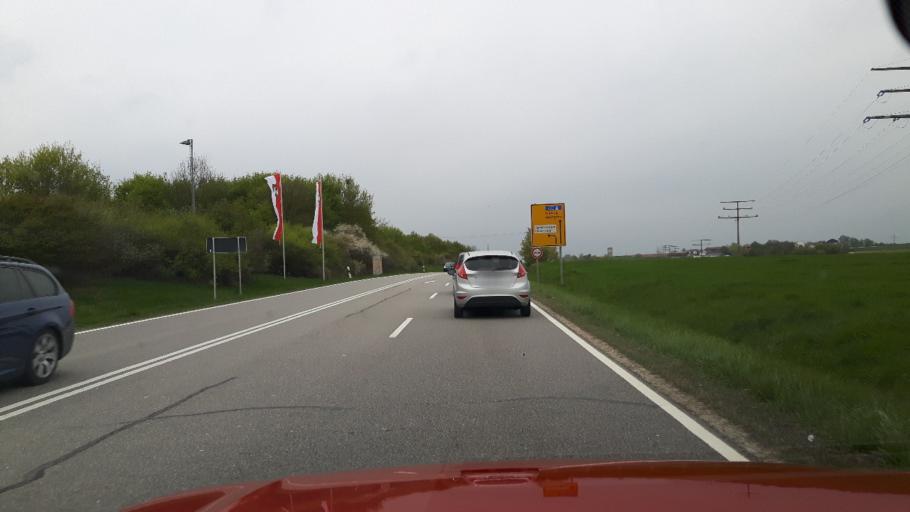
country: DE
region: Bavaria
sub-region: Upper Bavaria
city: Eichstaett
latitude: 48.8920
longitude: 11.2136
